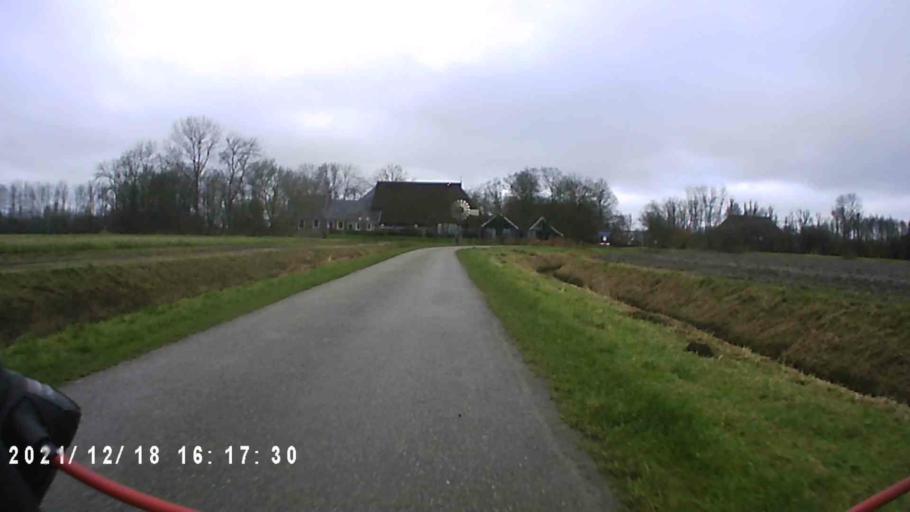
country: NL
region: Friesland
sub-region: Gemeente Dongeradeel
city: Anjum
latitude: 53.3752
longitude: 6.0580
